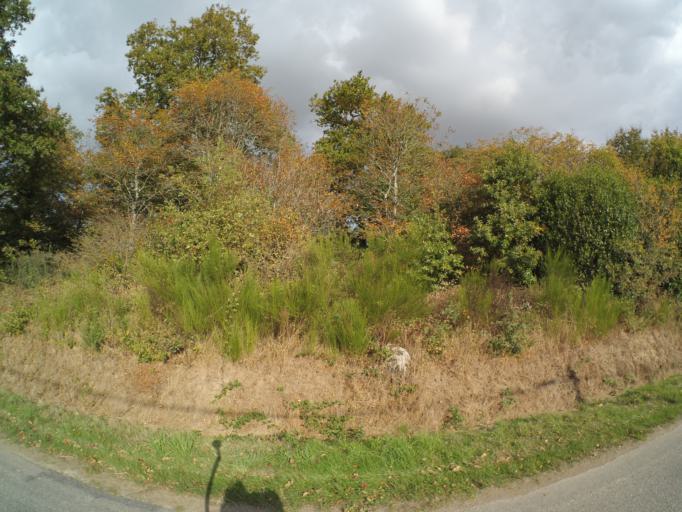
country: FR
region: Pays de la Loire
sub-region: Departement de la Loire-Atlantique
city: Remouille
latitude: 47.0683
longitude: -1.3558
